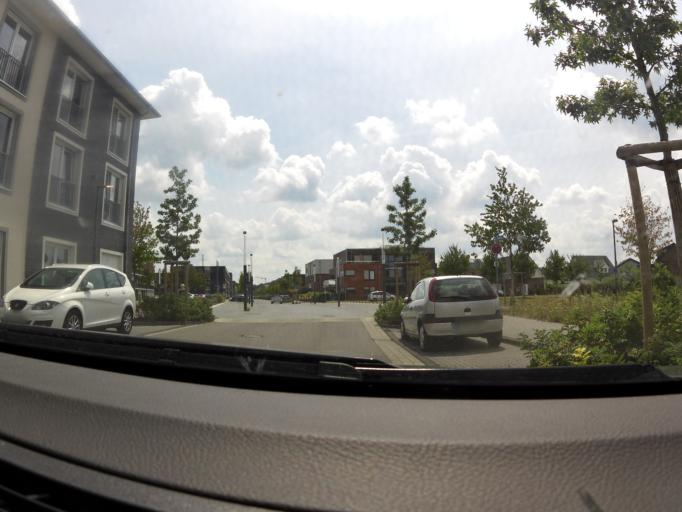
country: DE
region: North Rhine-Westphalia
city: Geldern
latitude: 51.5137
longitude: 6.3172
